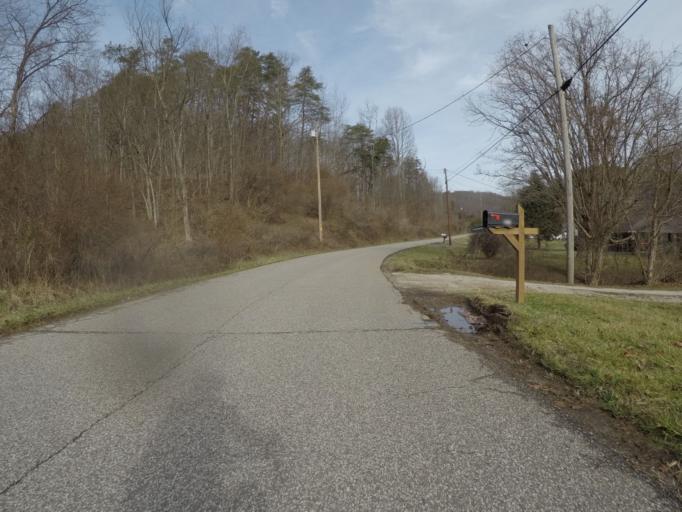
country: US
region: West Virginia
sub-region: Cabell County
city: Pea Ridge
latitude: 38.3564
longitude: -82.3729
